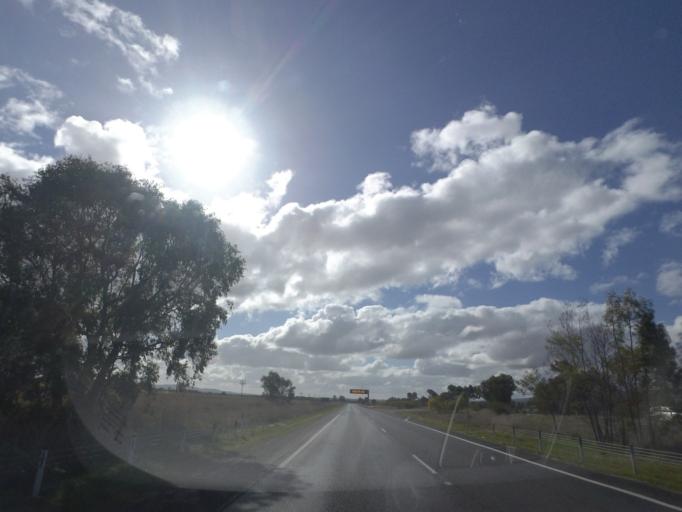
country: AU
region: New South Wales
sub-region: Greater Hume Shire
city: Jindera
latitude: -35.9467
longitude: 147.0035
